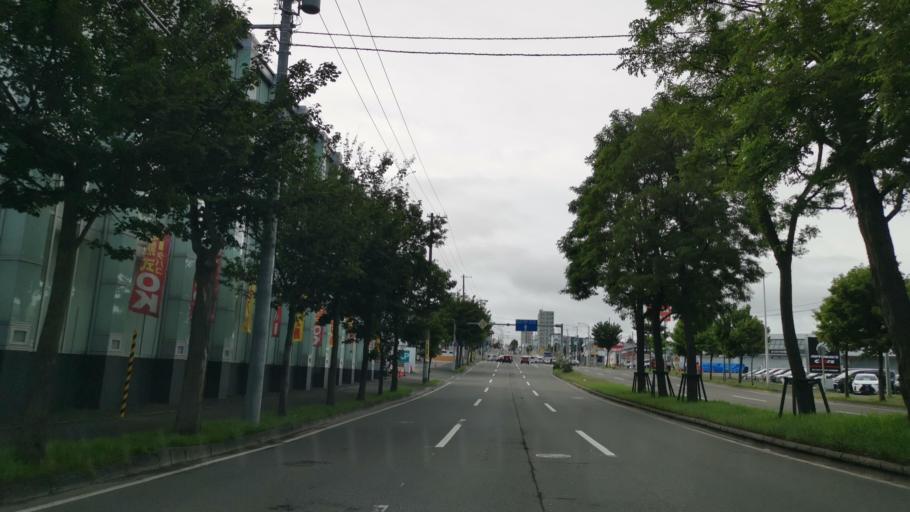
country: JP
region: Hokkaido
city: Sapporo
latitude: 43.0222
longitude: 141.3826
